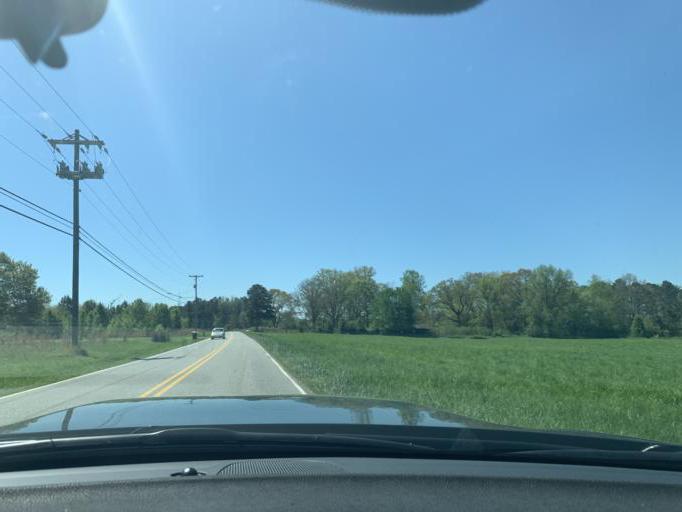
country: US
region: Georgia
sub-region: Forsyth County
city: Cumming
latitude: 34.1736
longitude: -84.1682
